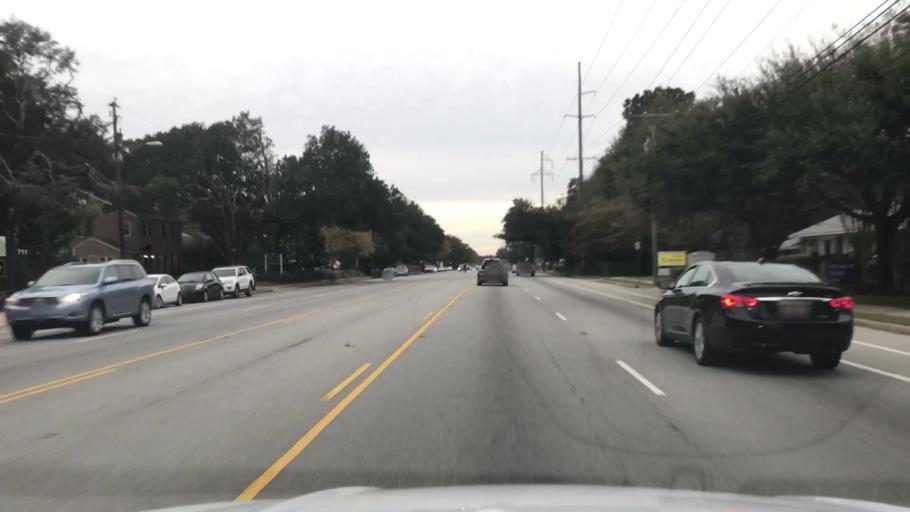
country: US
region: South Carolina
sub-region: Charleston County
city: Charleston
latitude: 32.7873
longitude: -79.9818
